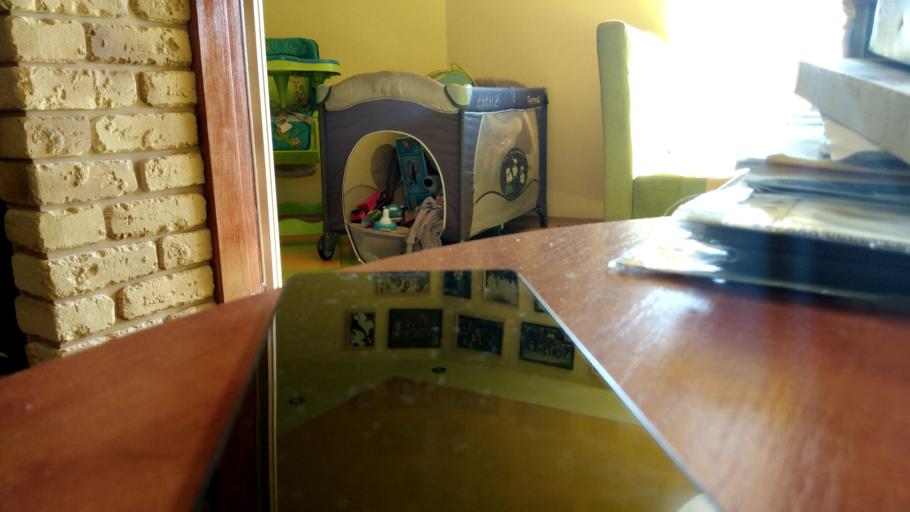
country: RU
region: Penza
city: Serdobsk
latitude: 52.3291
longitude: 44.3776
